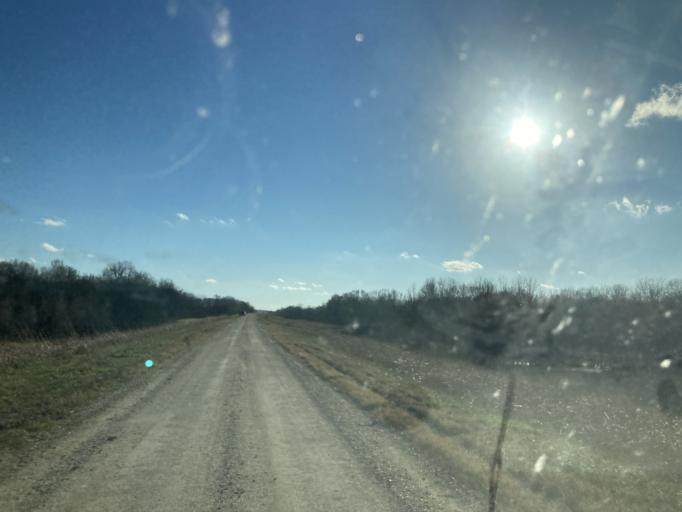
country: US
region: Mississippi
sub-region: Yazoo County
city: Yazoo City
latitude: 32.9247
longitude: -90.5512
